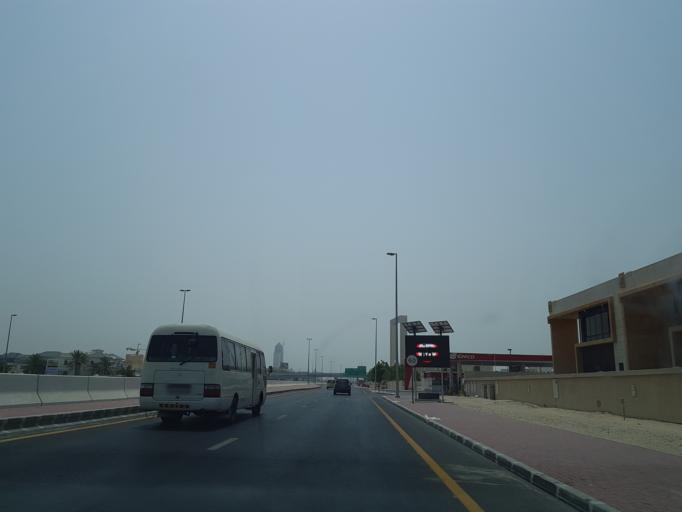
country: AE
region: Ash Shariqah
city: Sharjah
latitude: 25.2419
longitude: 55.2906
